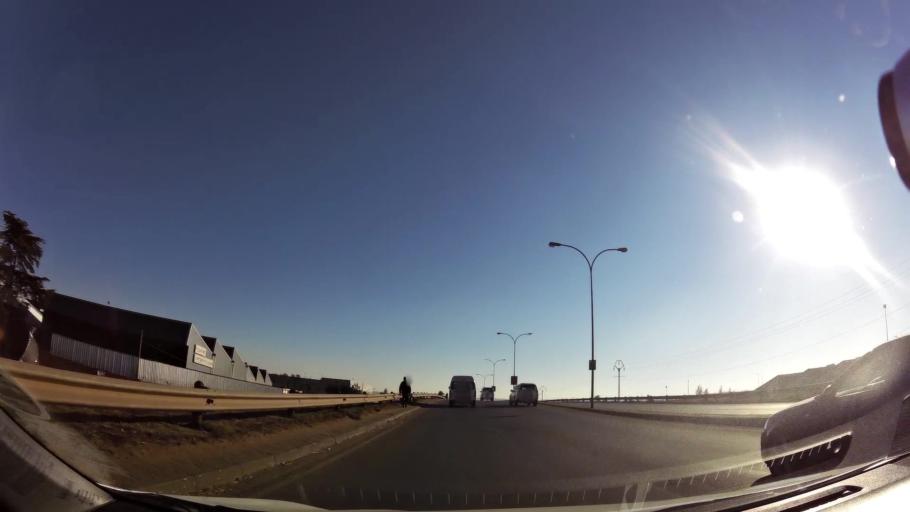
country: ZA
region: Gauteng
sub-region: Ekurhuleni Metropolitan Municipality
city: Germiston
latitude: -26.2982
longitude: 28.1372
